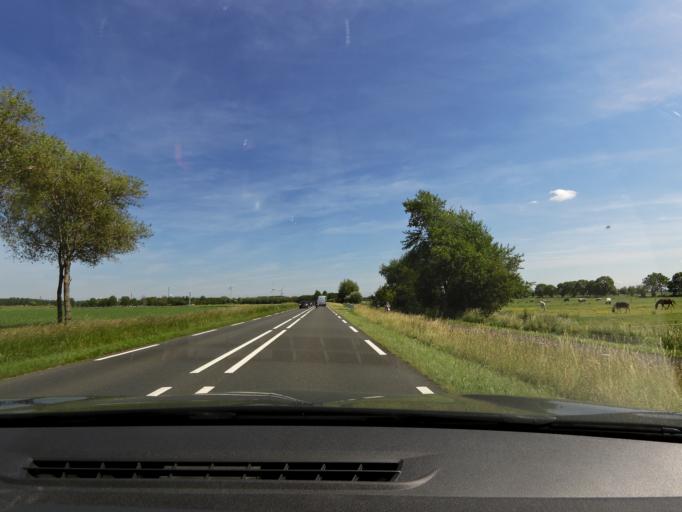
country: NL
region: South Holland
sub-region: Gemeente Brielle
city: Brielle
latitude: 51.8862
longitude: 4.2063
